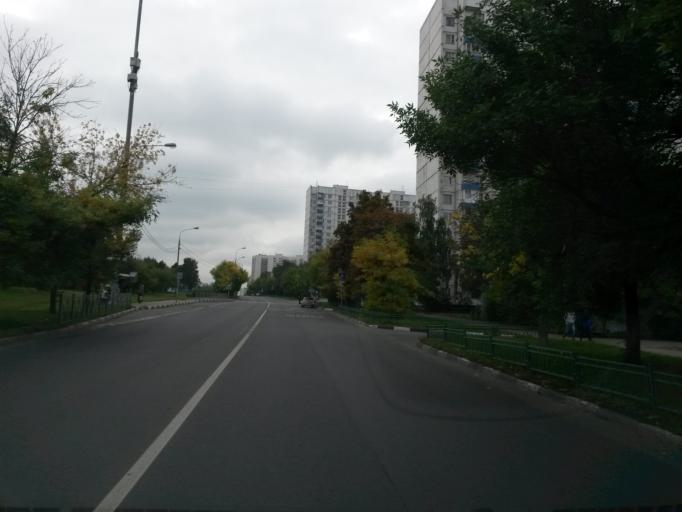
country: RU
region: Moscow
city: Orekhovo-Borisovo
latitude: 55.6181
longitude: 37.7280
